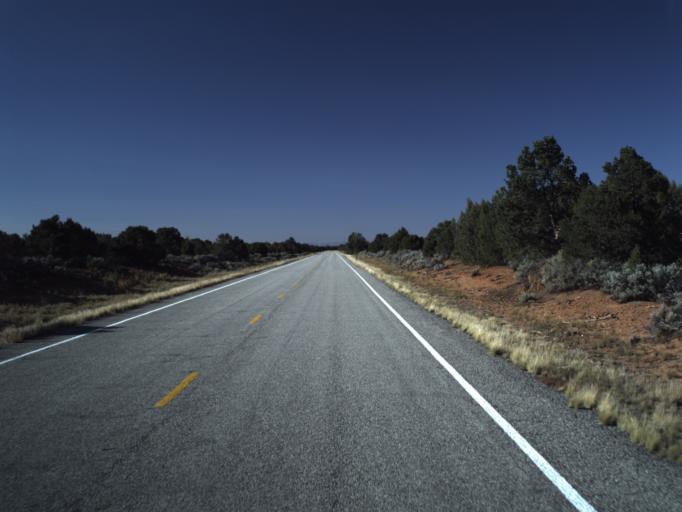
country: US
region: Utah
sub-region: San Juan County
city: Blanding
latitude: 37.5666
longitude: -109.9268
